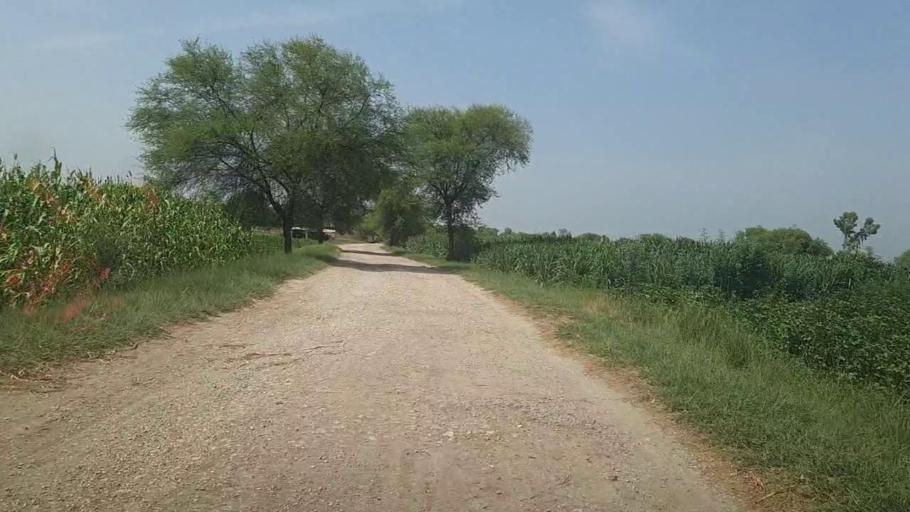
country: PK
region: Sindh
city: Ubauro
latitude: 28.1776
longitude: 69.8150
